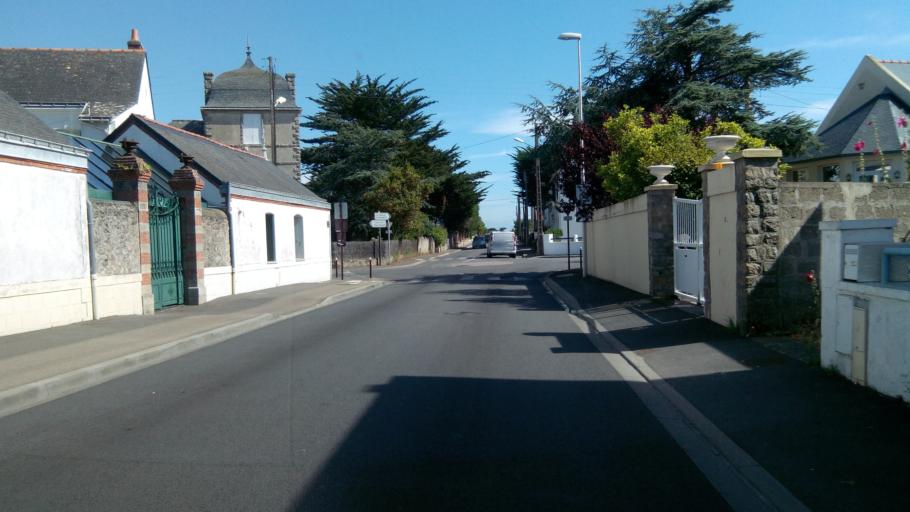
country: FR
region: Pays de la Loire
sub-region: Departement de la Loire-Atlantique
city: Le Croisic
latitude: 47.2883
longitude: -2.5101
